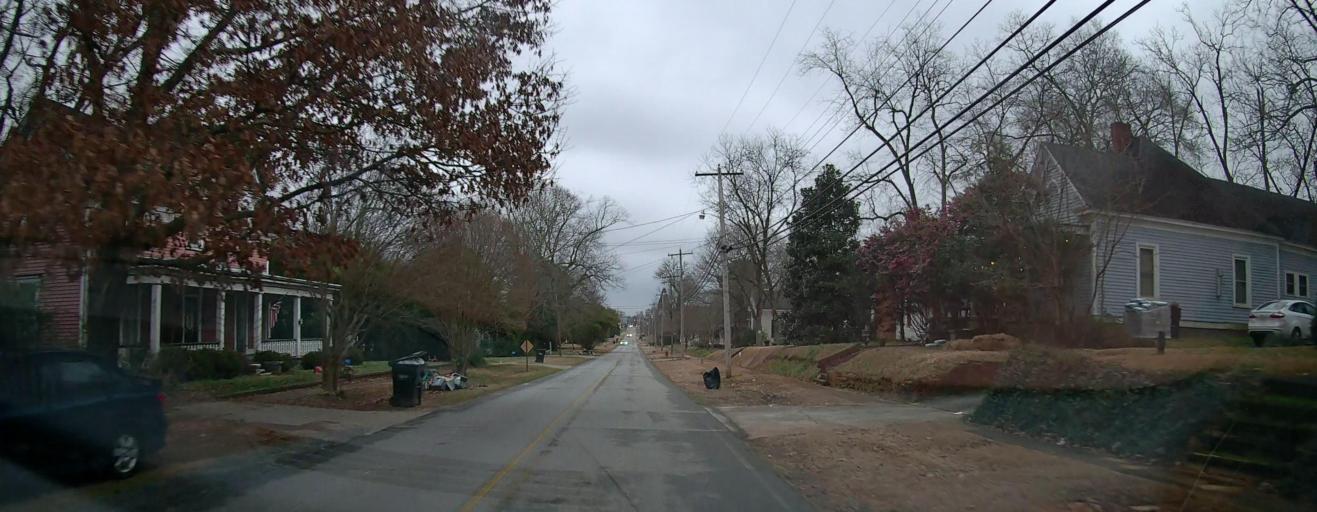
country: US
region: Georgia
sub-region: Lamar County
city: Barnesville
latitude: 33.0547
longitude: -84.1627
